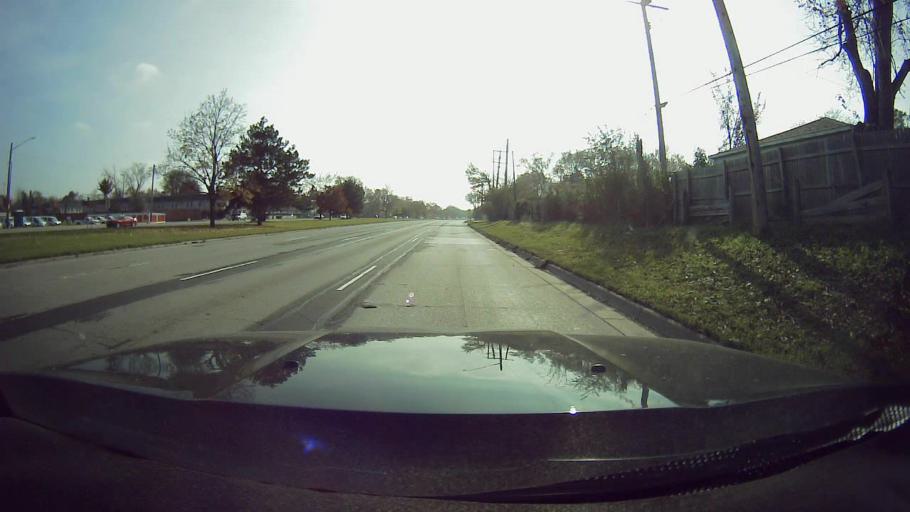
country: US
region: Michigan
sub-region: Wayne County
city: Redford
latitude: 42.4369
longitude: -83.2789
